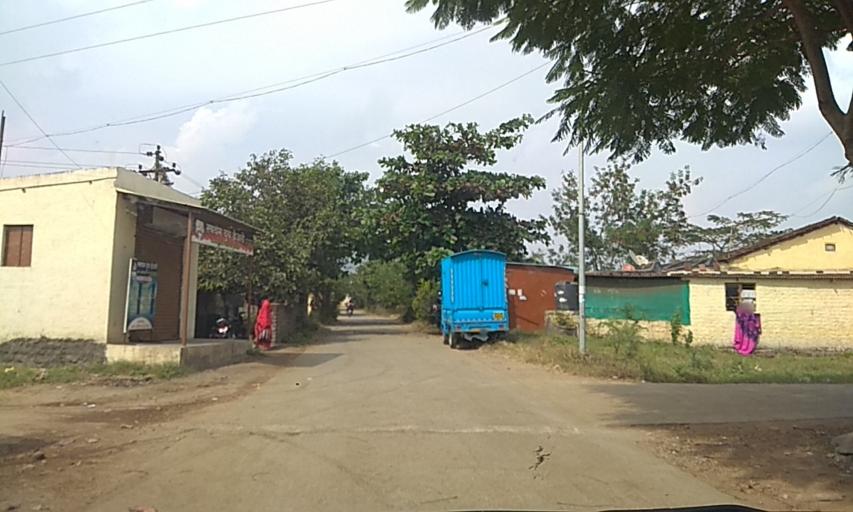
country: IN
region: Maharashtra
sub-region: Pune Division
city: Pimpri
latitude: 18.5813
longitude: 73.7072
